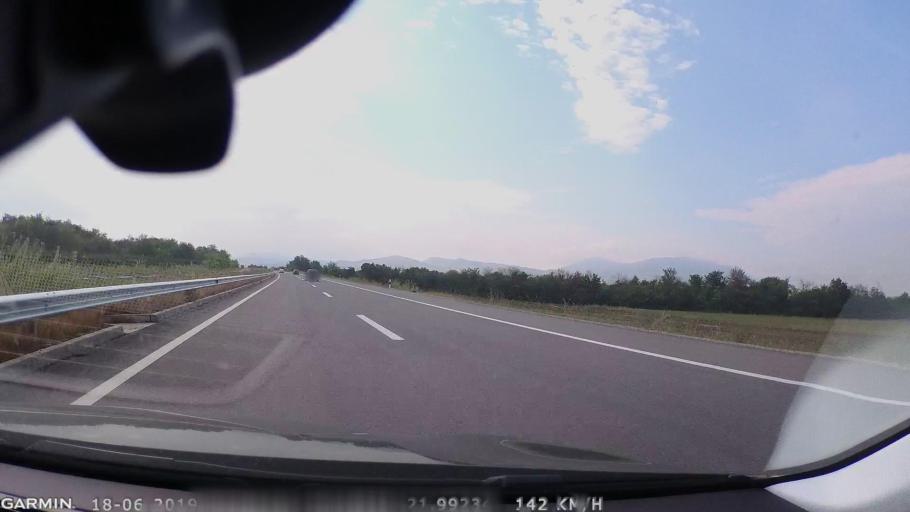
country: MK
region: Sveti Nikole
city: Sveti Nikole
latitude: 41.8437
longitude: 21.9773
